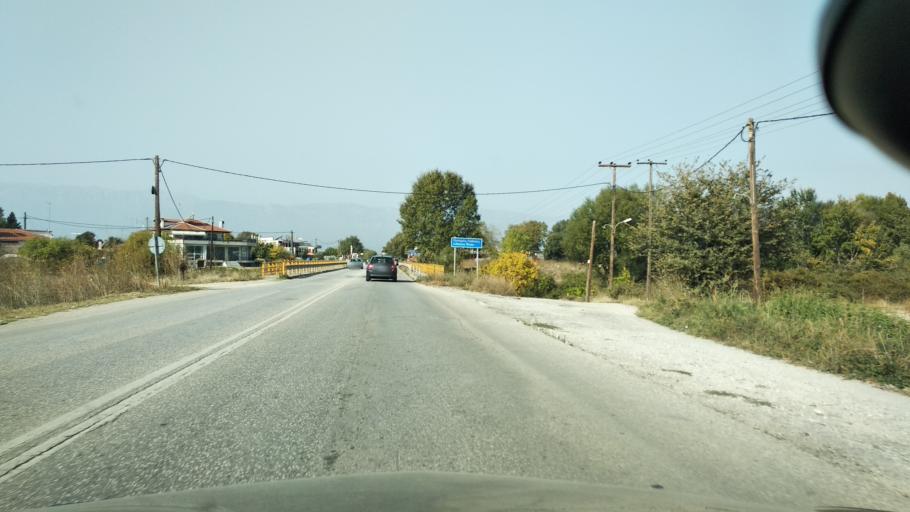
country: GR
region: Thessaly
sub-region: Trikala
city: Trikala
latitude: 39.5706
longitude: 21.7569
